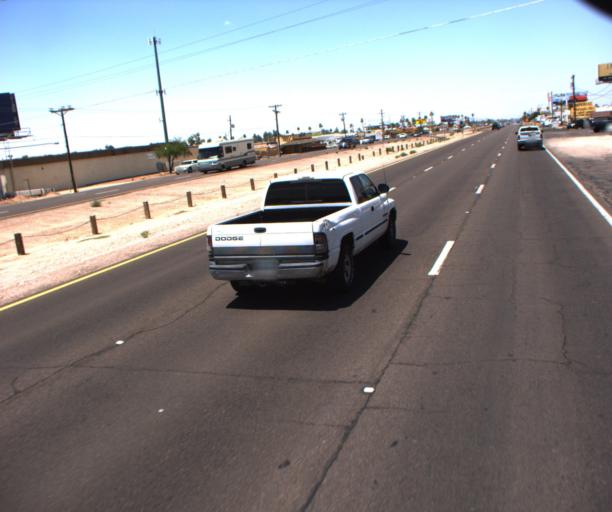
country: US
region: Arizona
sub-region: Pinal County
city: Apache Junction
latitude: 33.4154
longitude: -111.6216
